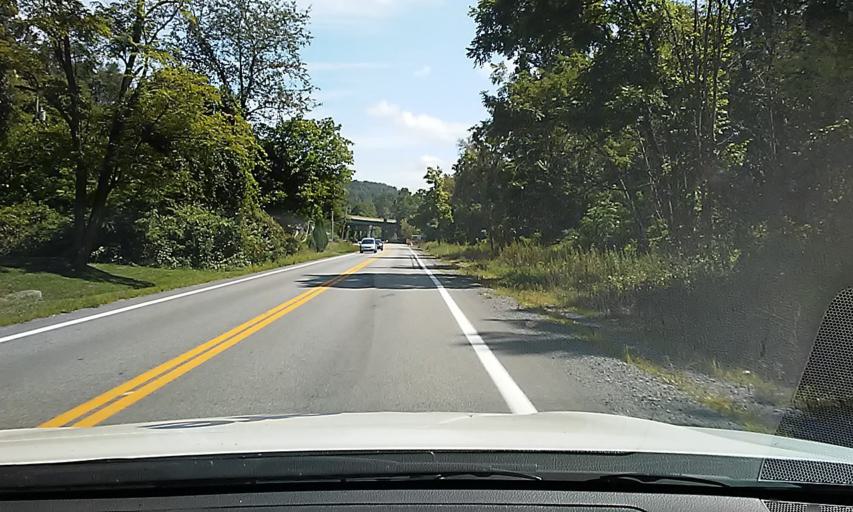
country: US
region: West Virginia
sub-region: Monongalia County
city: Star City
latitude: 39.6670
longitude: -80.0252
